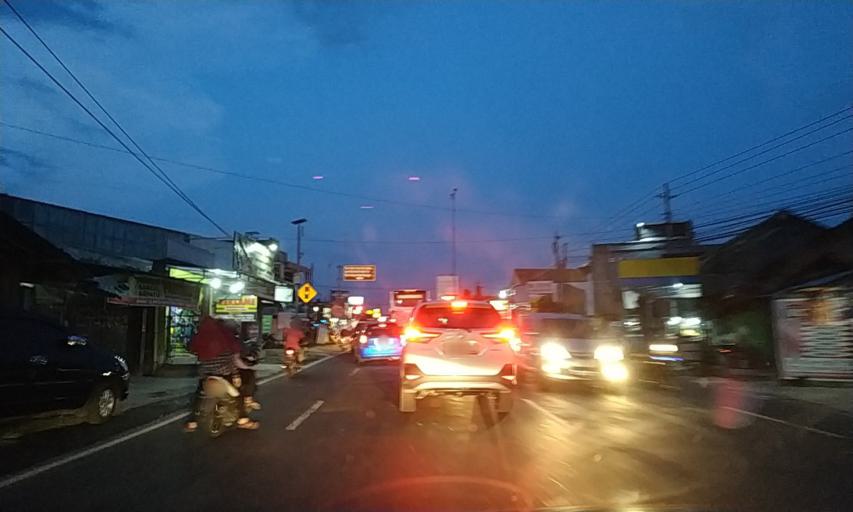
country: ID
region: Daerah Istimewa Yogyakarta
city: Godean
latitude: -7.8124
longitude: 110.2701
